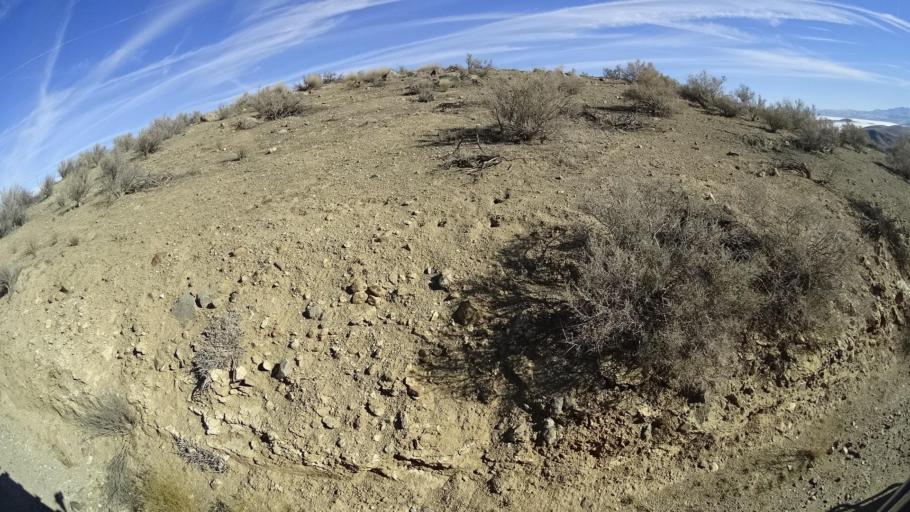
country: US
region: California
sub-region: Kern County
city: Maricopa
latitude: 35.0155
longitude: -119.4727
